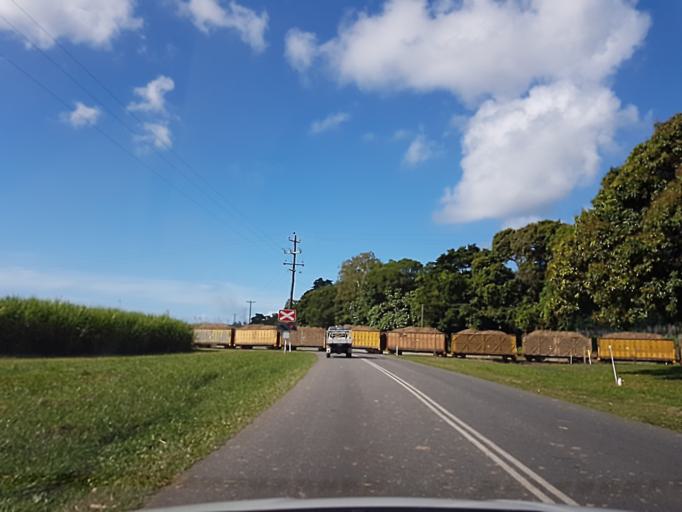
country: AU
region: Queensland
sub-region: Cairns
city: Port Douglas
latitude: -16.4744
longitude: 145.3522
